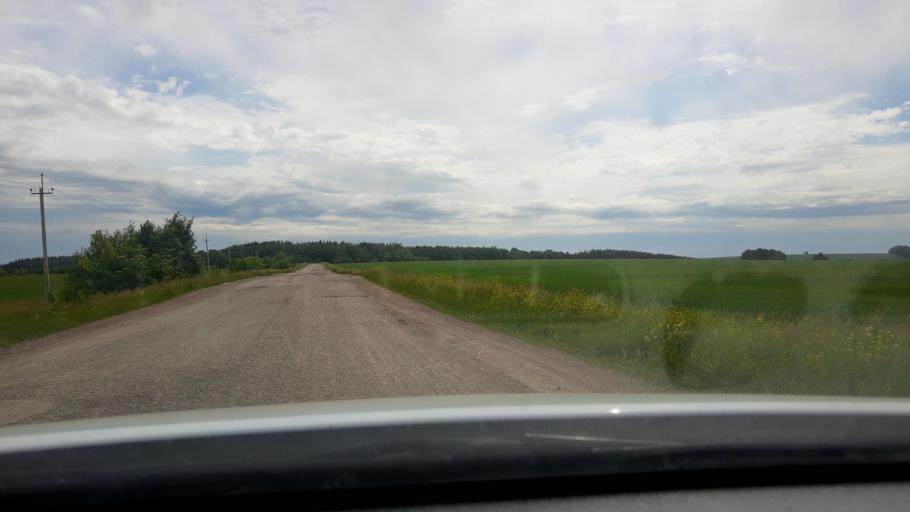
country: RU
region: Bashkortostan
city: Iglino
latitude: 54.7534
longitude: 56.5296
